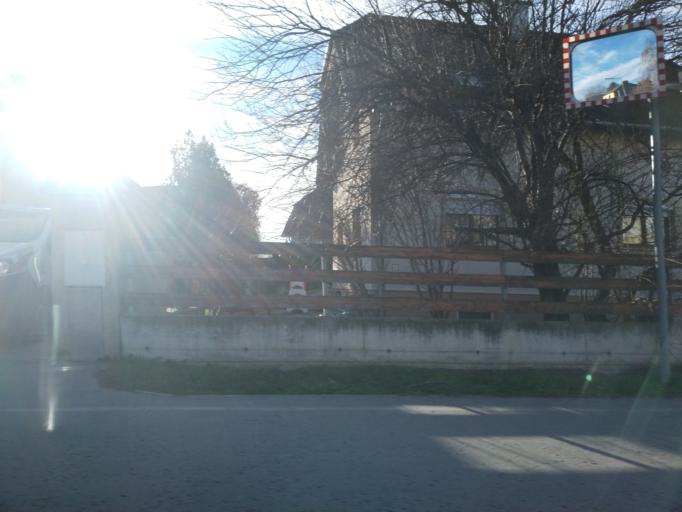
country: AT
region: Lower Austria
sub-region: Politischer Bezirk Baden
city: Bad Voslau
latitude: 47.9592
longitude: 16.2173
